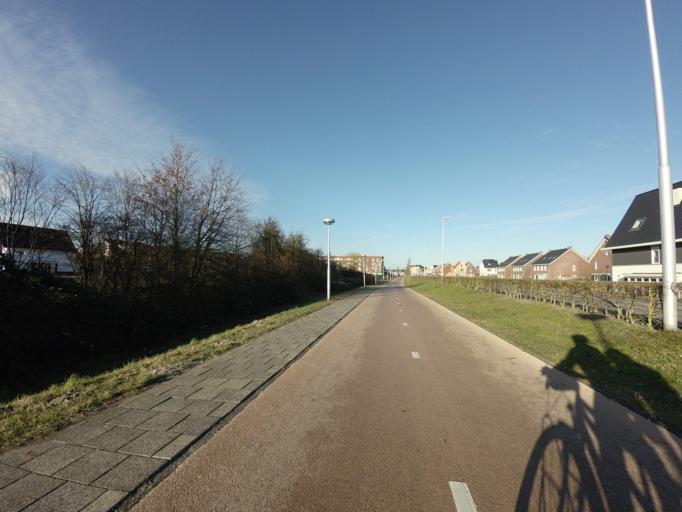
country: NL
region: Utrecht
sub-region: Stichtse Vecht
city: Spechtenkamp
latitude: 52.0875
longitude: 5.0121
